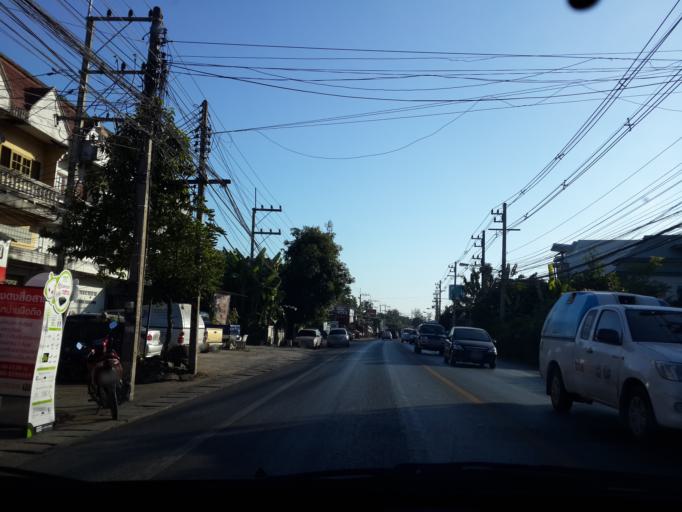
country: TH
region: Chiang Mai
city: Hang Dong
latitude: 18.6821
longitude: 98.9185
